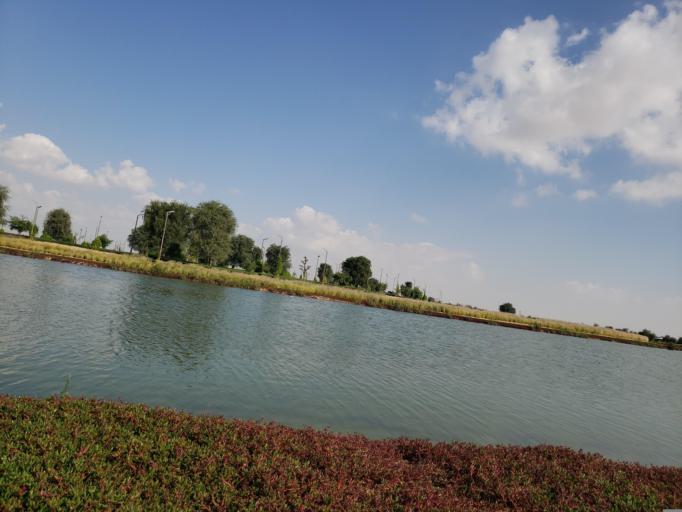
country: AE
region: Dubai
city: Dubai
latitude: 24.8526
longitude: 55.2479
